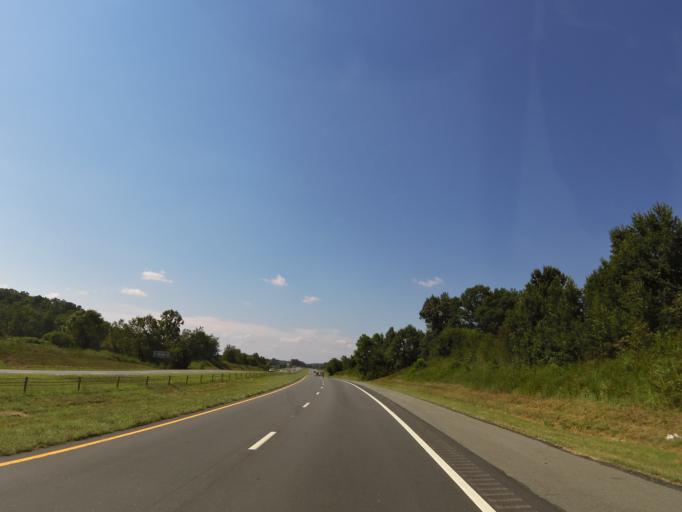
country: US
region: North Carolina
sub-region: Catawba County
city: Maiden
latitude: 35.5402
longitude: -81.2283
